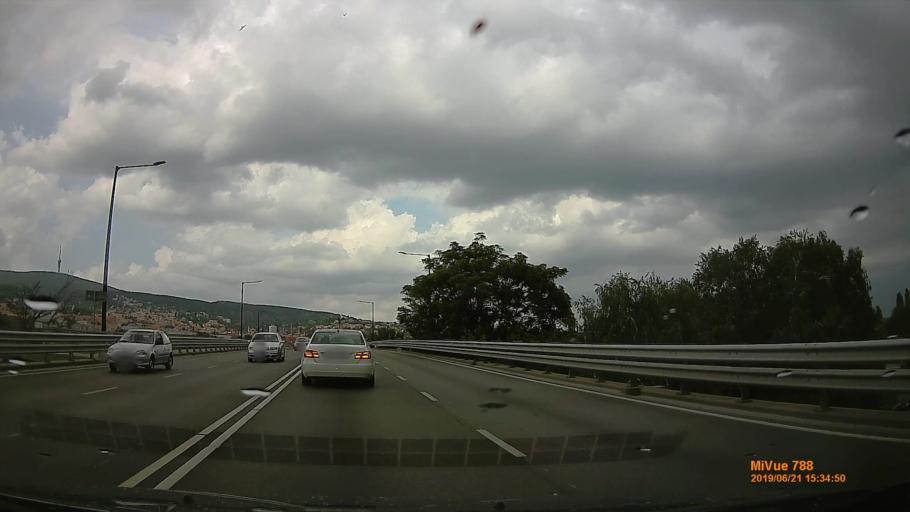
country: HU
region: Baranya
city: Pecs
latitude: 46.0665
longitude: 18.2320
